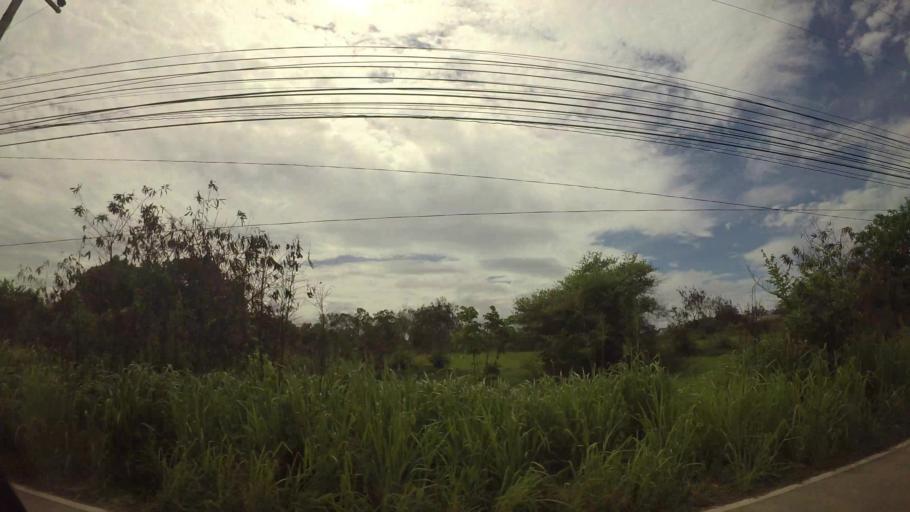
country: TH
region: Rayong
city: Rayong
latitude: 12.6629
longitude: 101.2845
